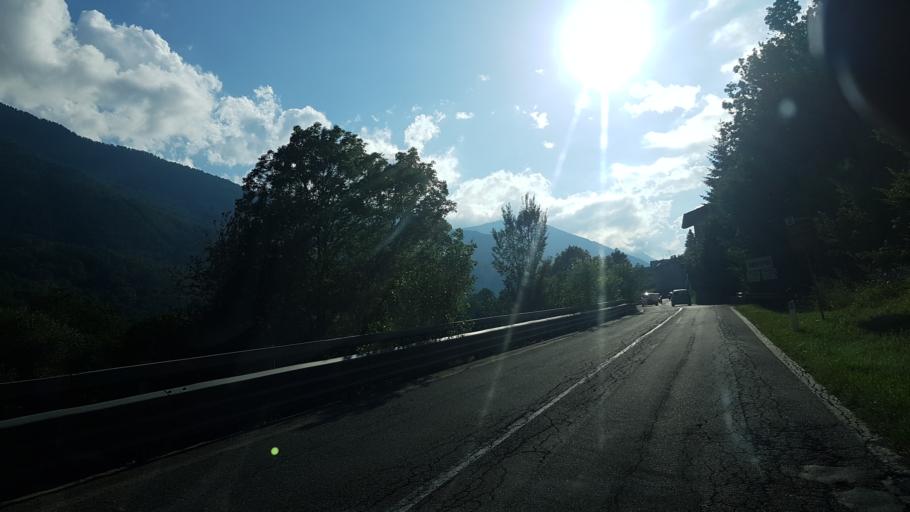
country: IT
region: Piedmont
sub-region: Provincia di Cuneo
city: Sampeyre
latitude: 44.5779
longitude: 7.2058
